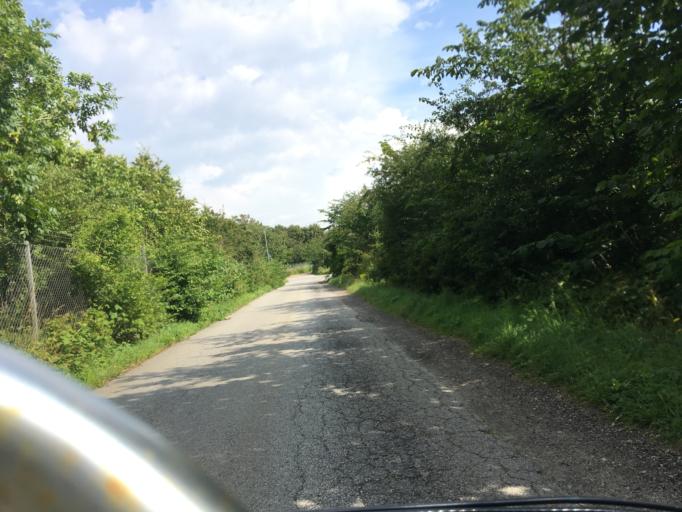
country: SE
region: Skane
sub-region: Lunds Kommun
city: Lund
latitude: 55.6937
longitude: 13.1669
